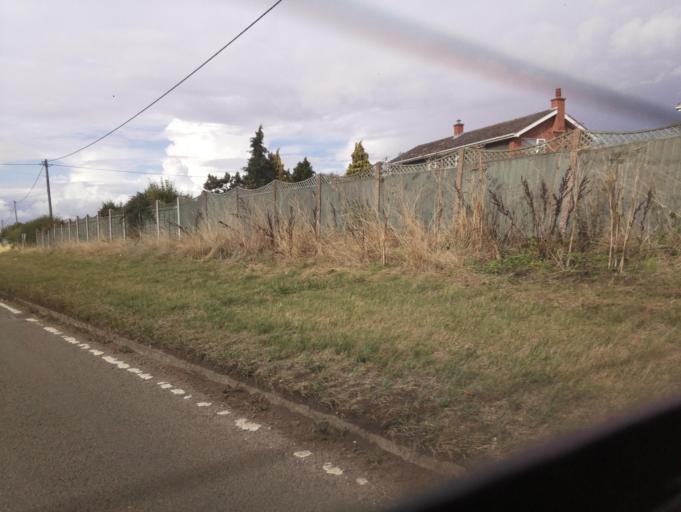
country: GB
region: England
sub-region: Telford and Wrekin
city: Madeley
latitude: 52.6097
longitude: -2.4102
